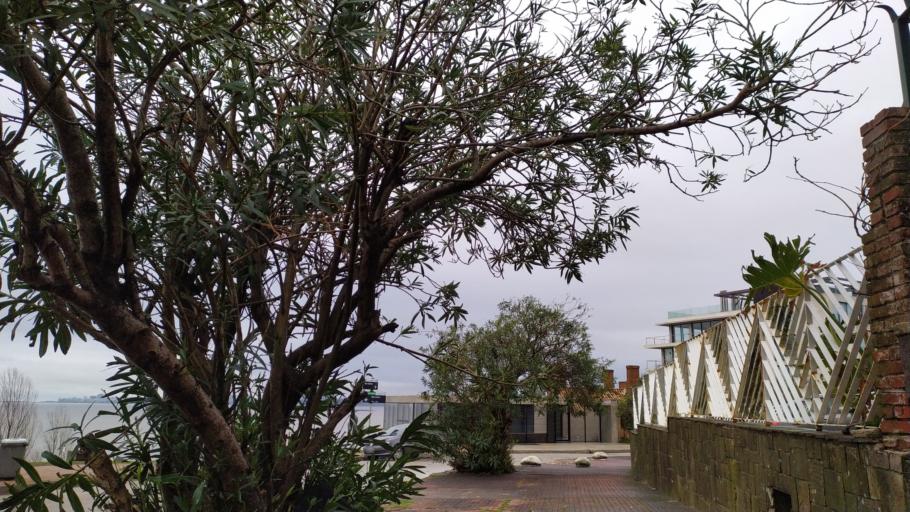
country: UY
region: Canelones
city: Paso de Carrasco
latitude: -34.8984
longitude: -56.0815
